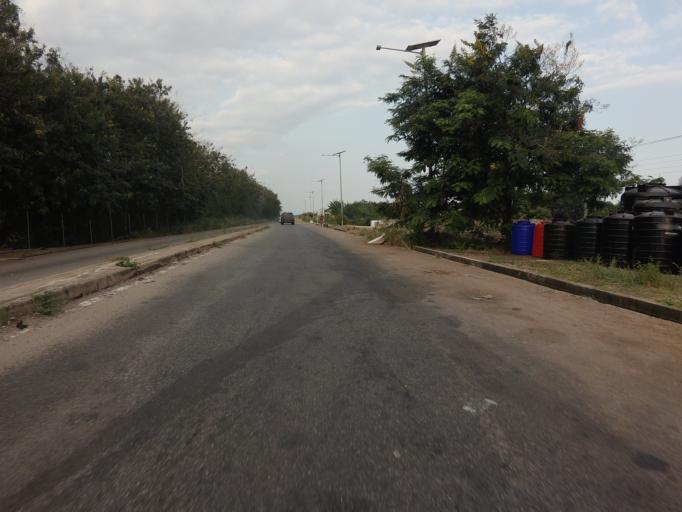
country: GH
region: Volta
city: Anloga
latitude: 6.0869
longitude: 0.5068
